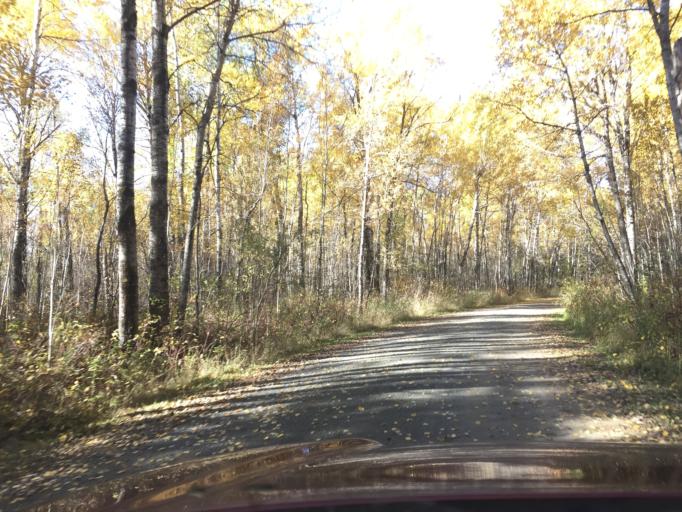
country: US
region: Minnesota
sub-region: Lake of the Woods County
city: Baudette
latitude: 48.2850
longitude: -94.5605
